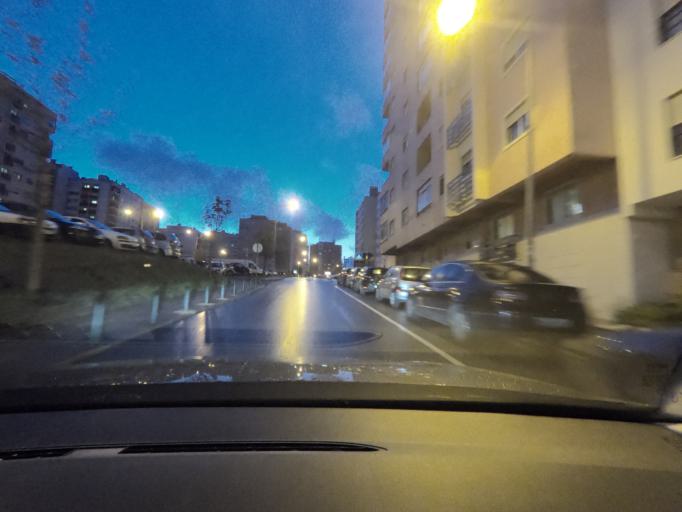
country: PT
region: Lisbon
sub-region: Sintra
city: Cacem
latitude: 38.7490
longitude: -9.2983
